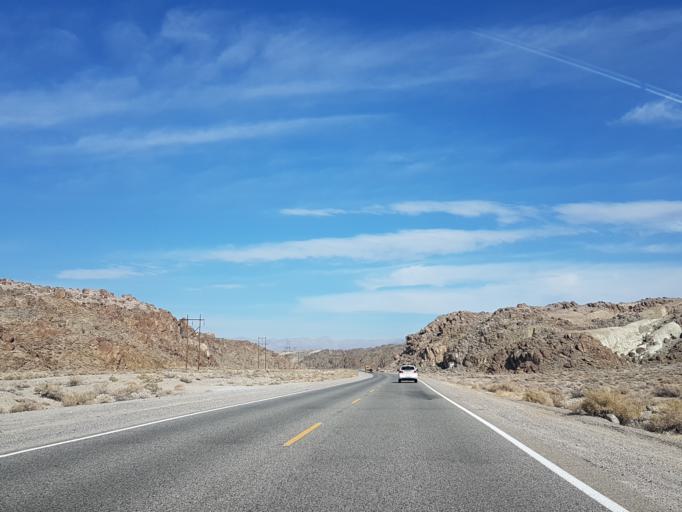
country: US
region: California
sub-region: San Bernardino County
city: Searles Valley
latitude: 35.6596
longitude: -117.4364
